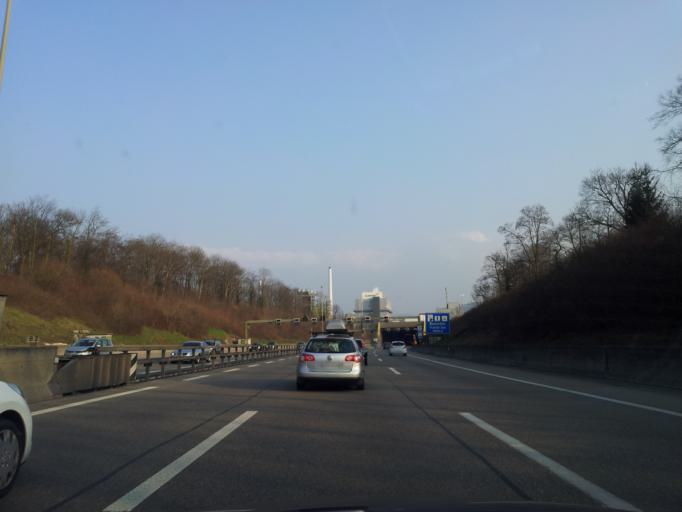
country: CH
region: Basel-Landschaft
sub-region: Bezirk Arlesheim
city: Muttenz
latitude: 47.5356
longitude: 7.6557
